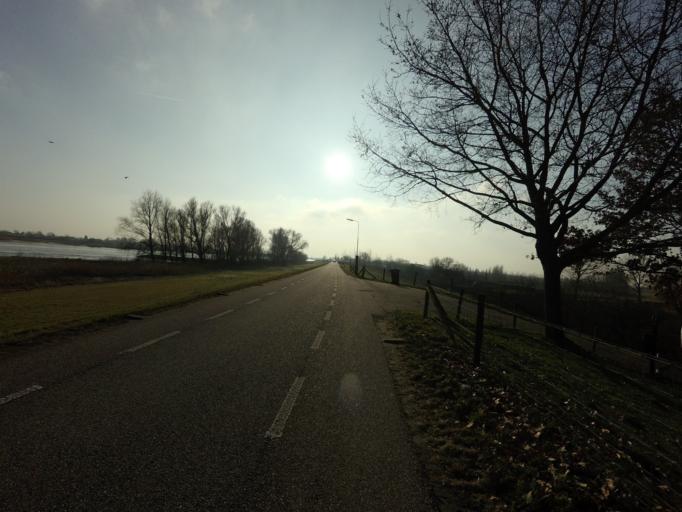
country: NL
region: Utrecht
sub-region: Gemeente Lopik
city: Lopik
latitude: 51.9626
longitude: 4.9320
